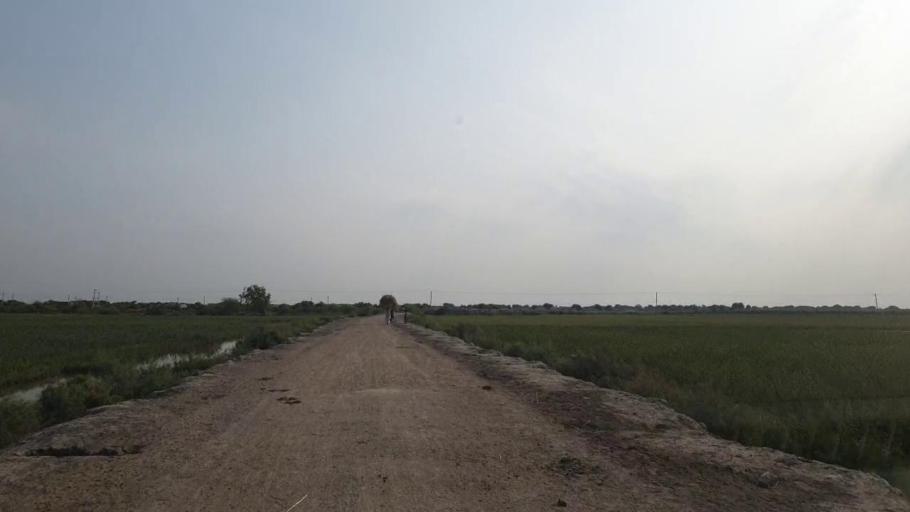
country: PK
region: Sindh
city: Kadhan
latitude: 24.4601
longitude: 68.8127
